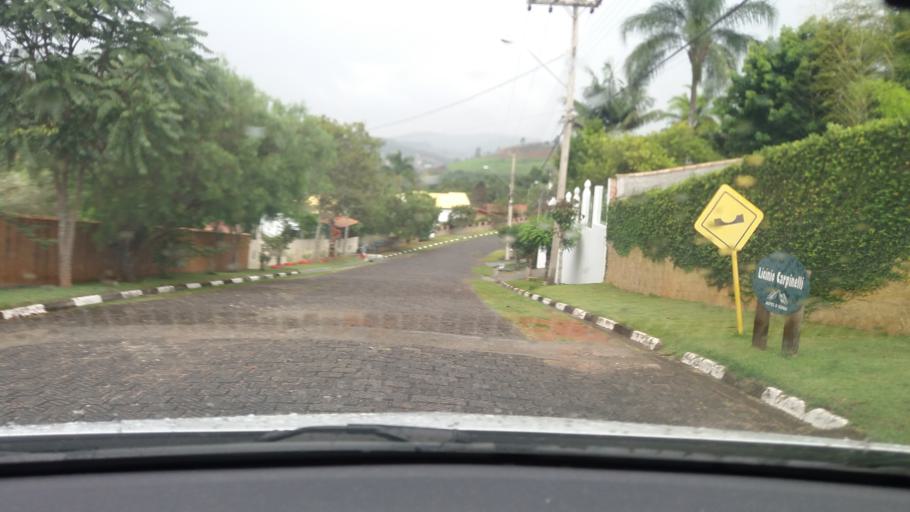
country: BR
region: Sao Paulo
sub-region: Bom Jesus Dos Perdoes
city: Bom Jesus dos Perdoes
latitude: -23.1667
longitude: -46.4529
